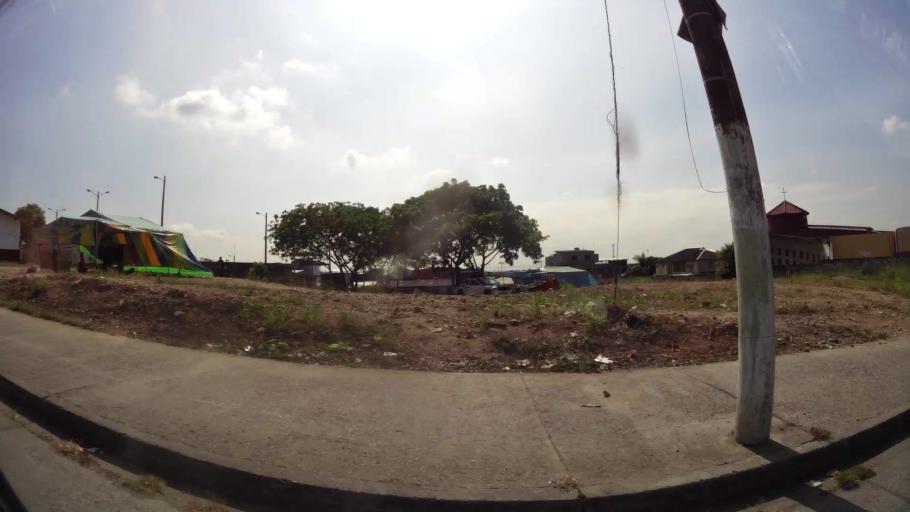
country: EC
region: Guayas
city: Eloy Alfaro
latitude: -2.1735
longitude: -79.8055
